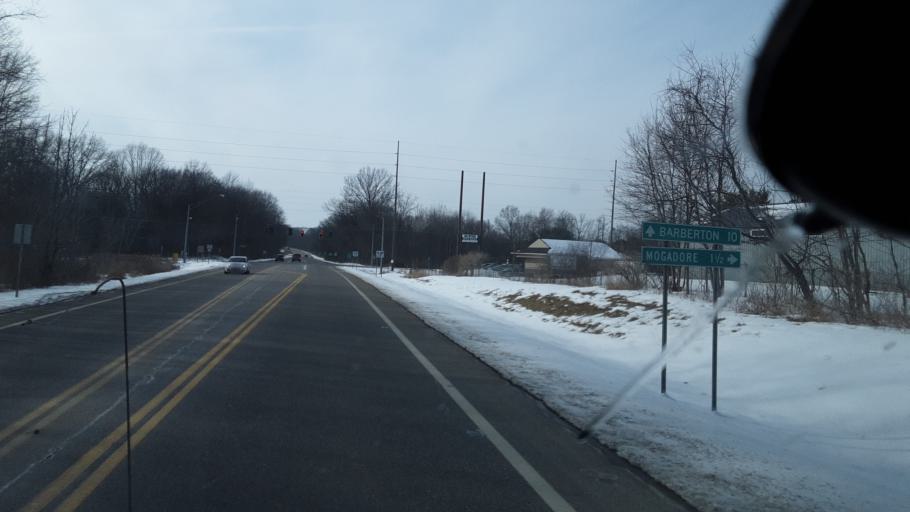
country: US
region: Ohio
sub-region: Summit County
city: Mogadore
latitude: 41.0288
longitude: -81.3916
